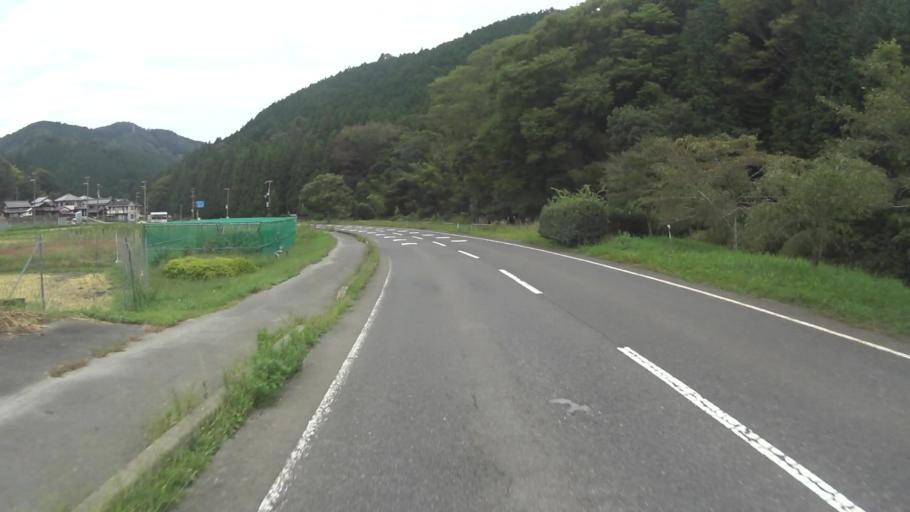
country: JP
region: Shiga Prefecture
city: Kusatsu
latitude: 34.8579
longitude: 135.9721
